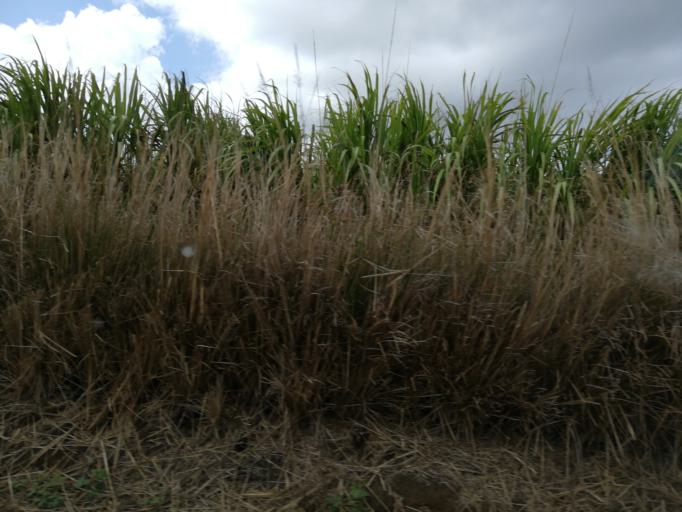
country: MU
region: Pamplemousses
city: Arsenal
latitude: -20.0919
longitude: 57.5434
